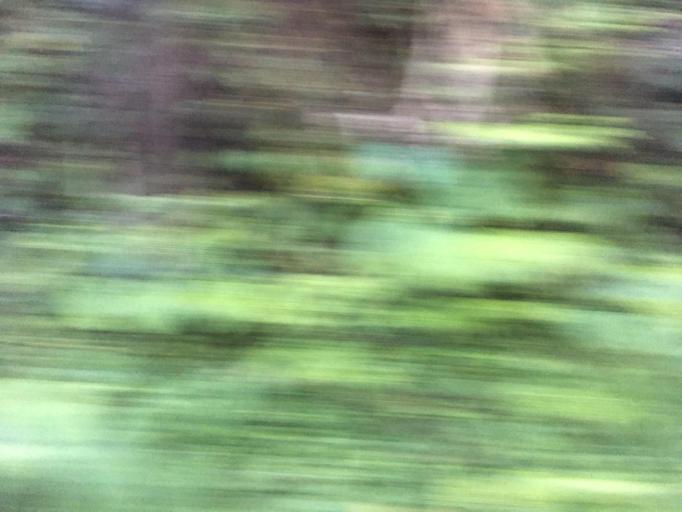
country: TW
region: Taiwan
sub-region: Yilan
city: Yilan
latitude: 24.5420
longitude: 121.5112
